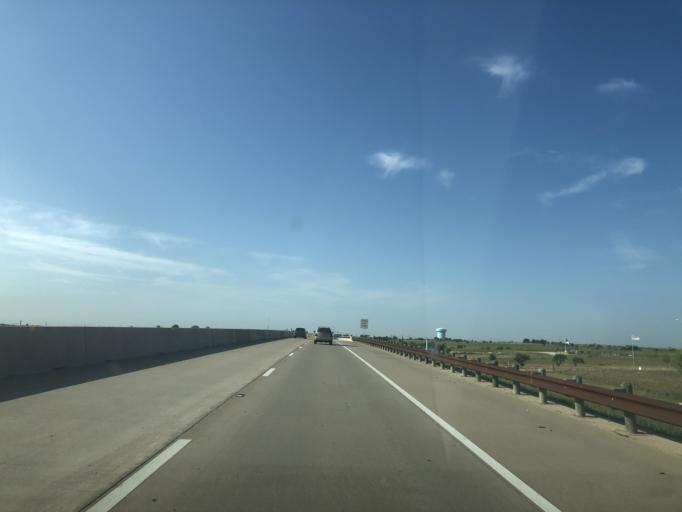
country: US
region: Texas
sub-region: Tarrant County
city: Crowley
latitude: 32.6168
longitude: -97.4127
